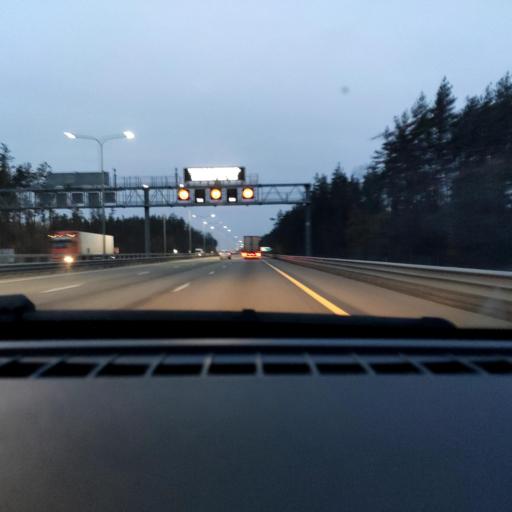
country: RU
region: Voronezj
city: Somovo
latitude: 51.7027
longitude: 39.3053
